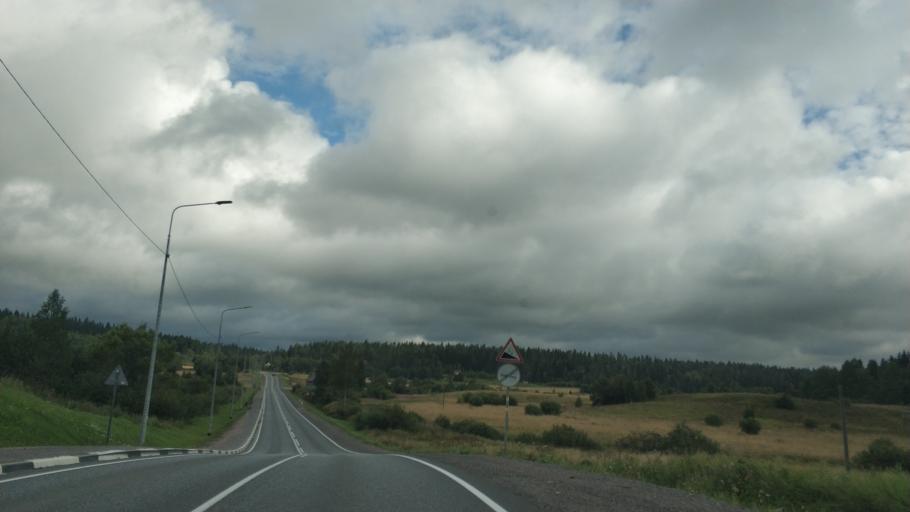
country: RU
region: Republic of Karelia
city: Khelyulya
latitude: 61.7590
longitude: 30.6573
